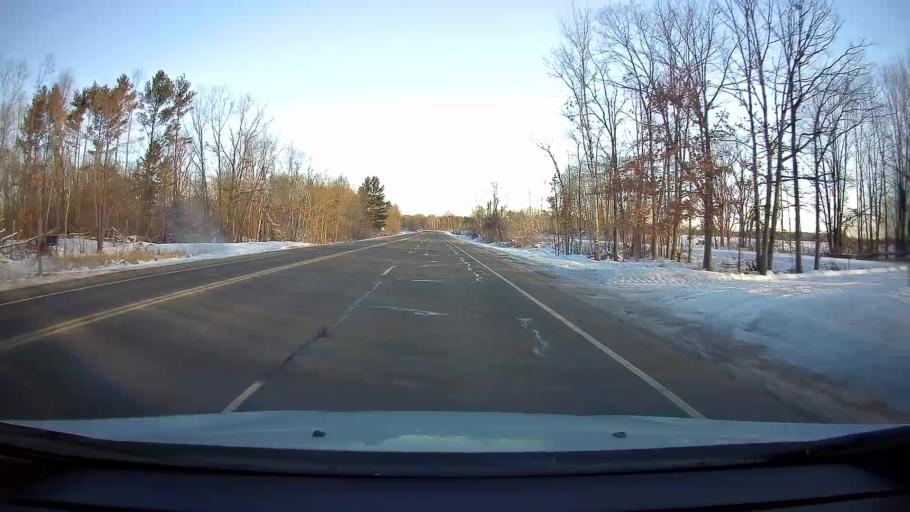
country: US
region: Wisconsin
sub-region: Barron County
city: Turtle Lake
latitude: 45.4264
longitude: -92.1296
